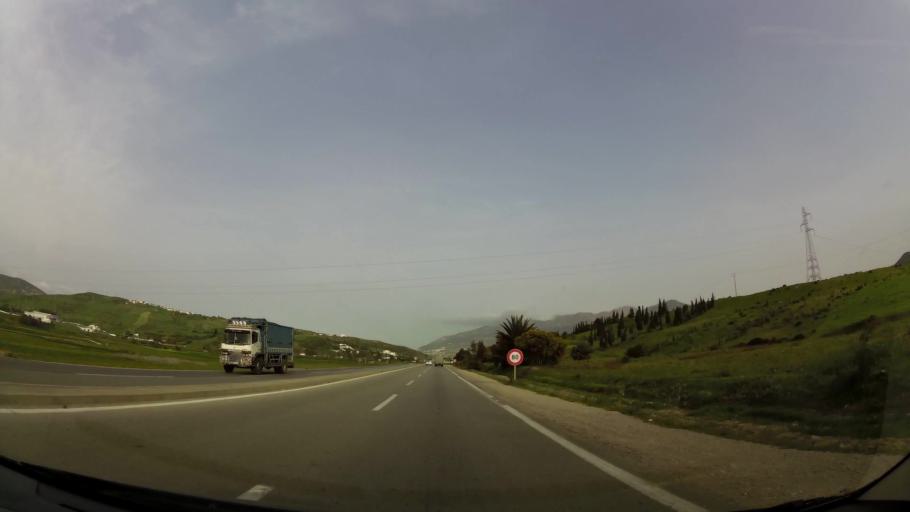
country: MA
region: Tanger-Tetouan
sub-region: Tetouan
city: Saddina
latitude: 35.5608
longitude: -5.4716
